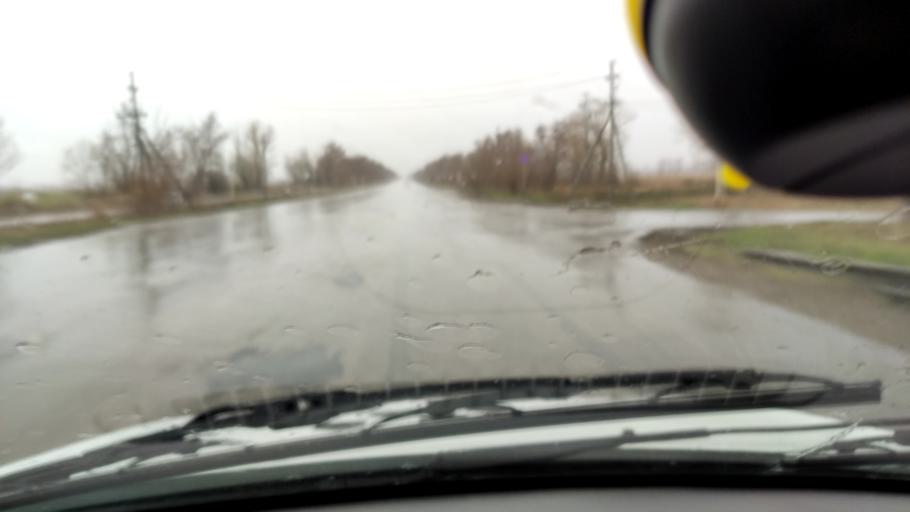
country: RU
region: Samara
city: Tol'yatti
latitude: 53.5864
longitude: 49.4051
